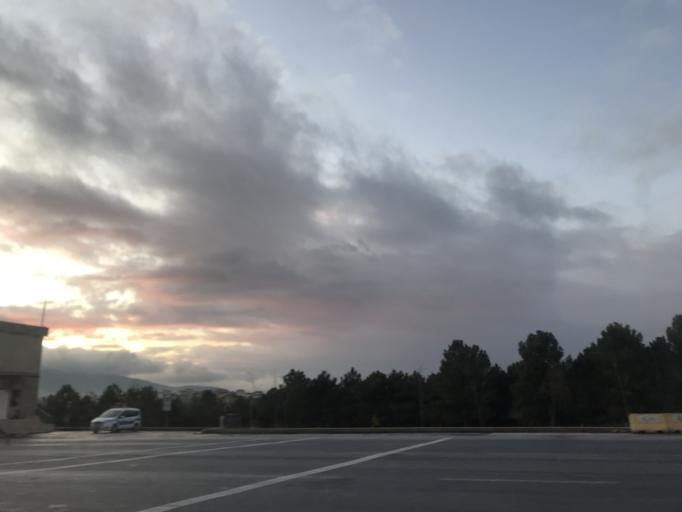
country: TR
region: Istanbul
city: Sultanbeyli
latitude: 40.9546
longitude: 29.3159
